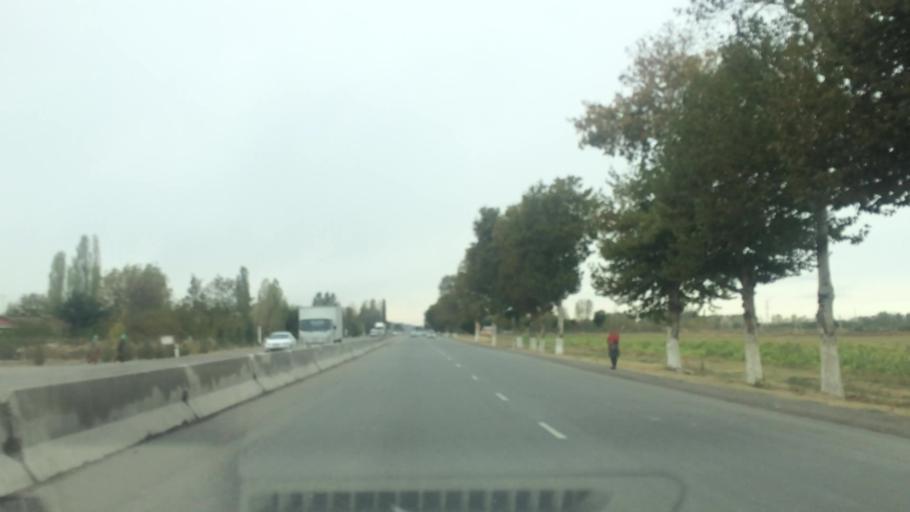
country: UZ
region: Samarqand
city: Jomboy
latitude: 39.7182
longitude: 67.1133
